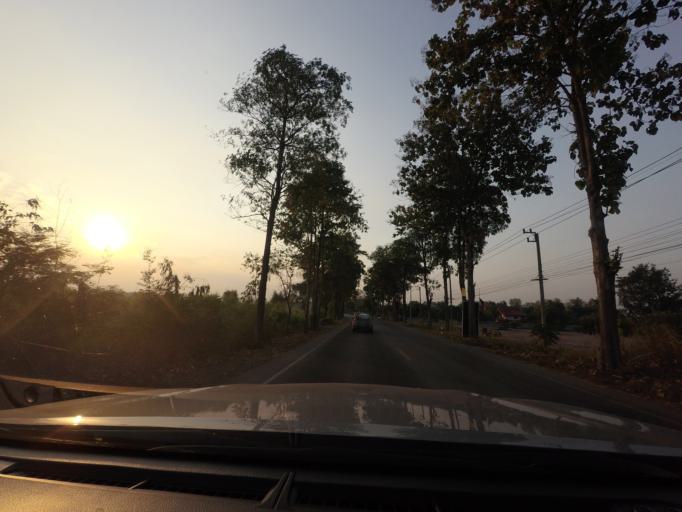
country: TH
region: Phitsanulok
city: Wang Thong
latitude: 16.7366
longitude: 100.4472
